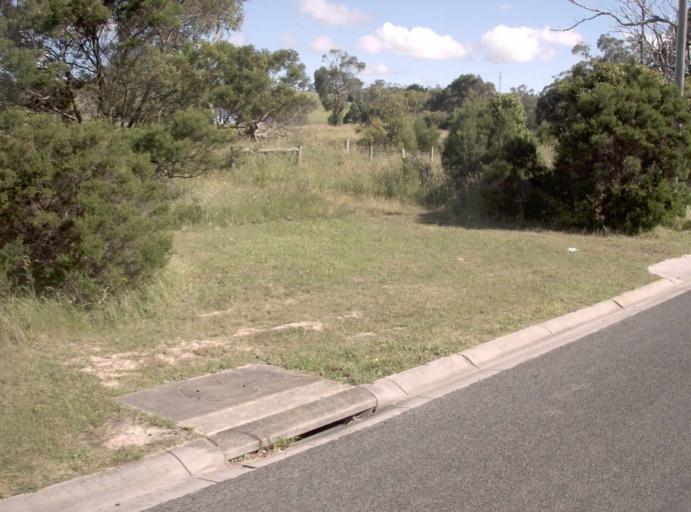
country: AU
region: Victoria
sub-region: Bass Coast
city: North Wonthaggi
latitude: -38.4100
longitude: 145.5287
